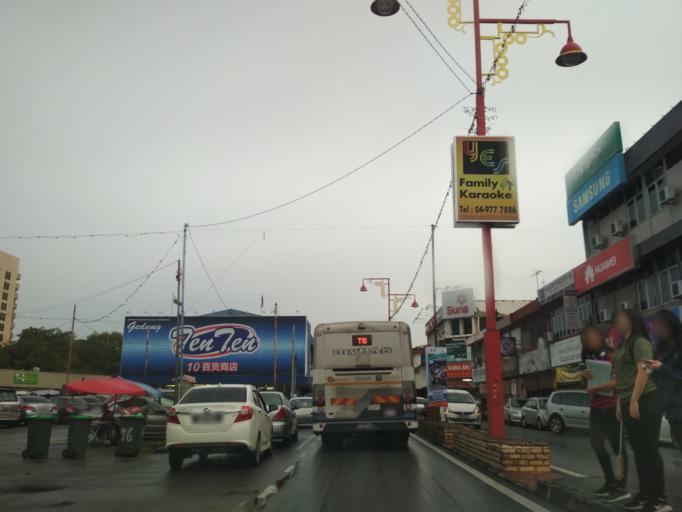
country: MY
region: Perlis
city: Kangar
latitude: 6.4366
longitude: 100.1909
